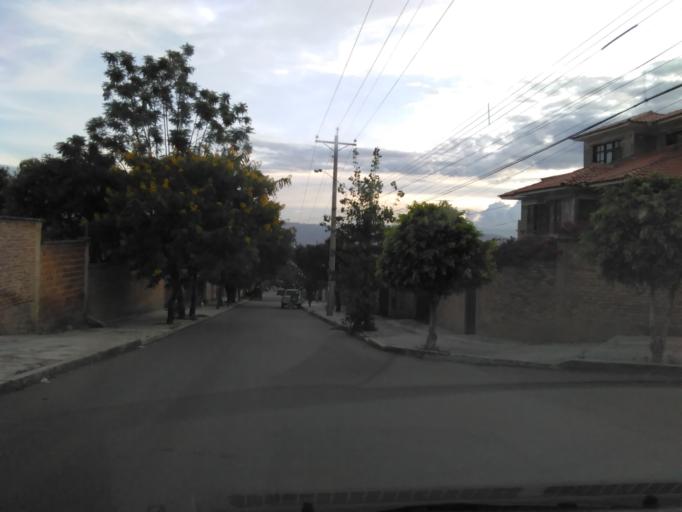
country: BO
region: Cochabamba
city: Cochabamba
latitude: -17.3588
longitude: -66.1611
